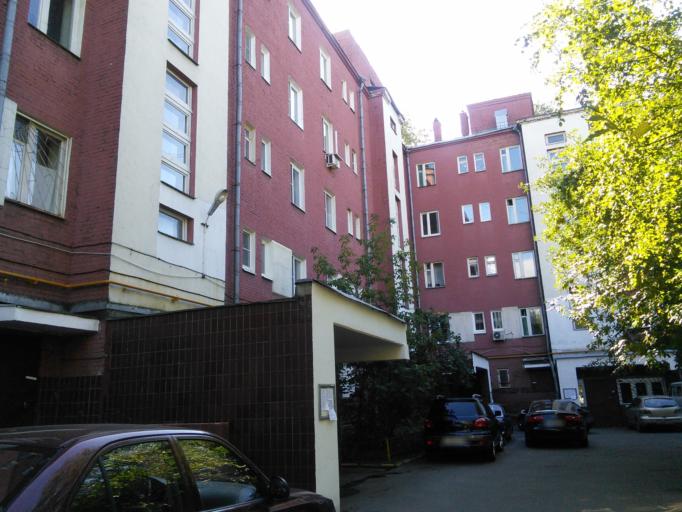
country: RU
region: Moscow
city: Lefortovo
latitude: 55.7860
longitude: 37.7149
